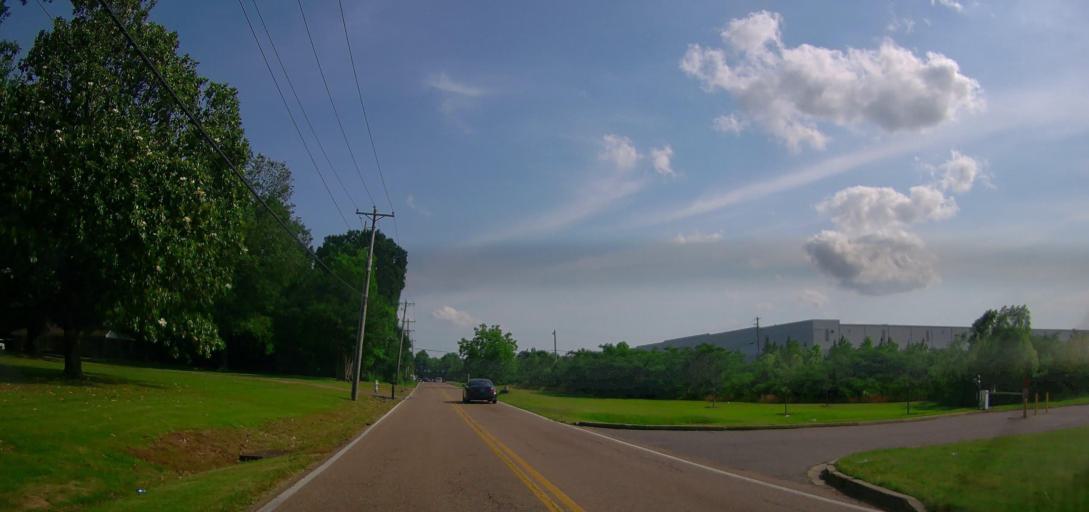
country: US
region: Mississippi
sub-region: De Soto County
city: Olive Branch
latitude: 35.0090
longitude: -89.8487
